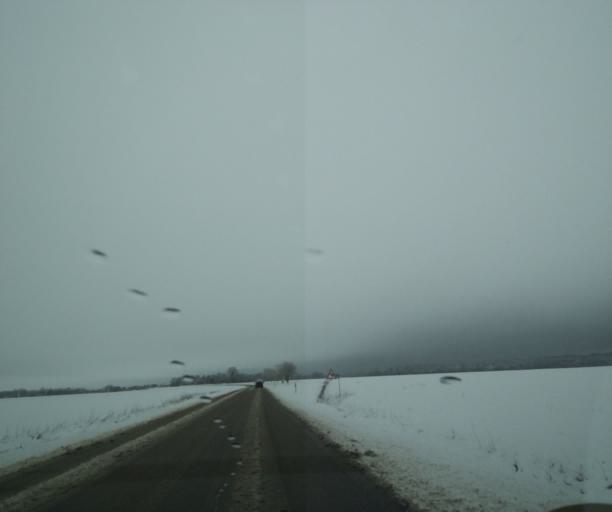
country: FR
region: Champagne-Ardenne
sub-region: Departement de la Haute-Marne
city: Wassy
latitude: 48.5353
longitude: 4.9247
